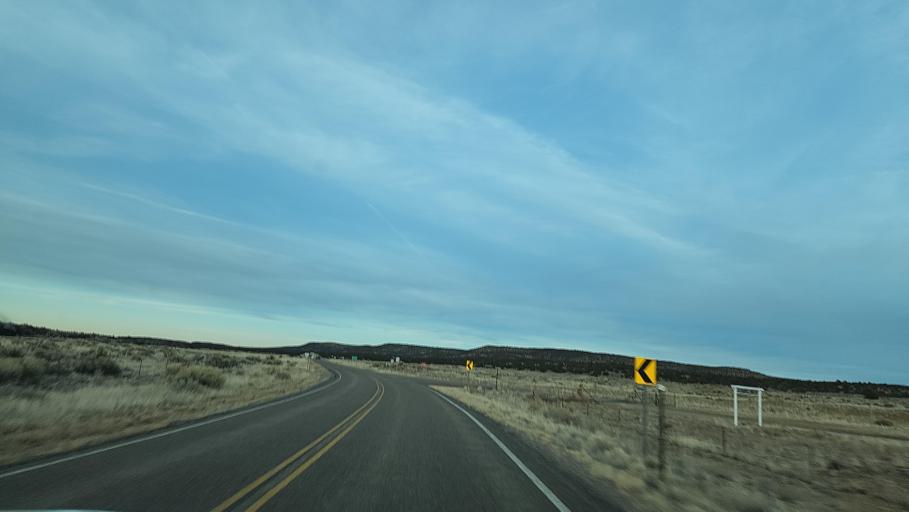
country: US
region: New Mexico
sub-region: Cibola County
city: Grants
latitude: 34.7109
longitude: -107.9894
